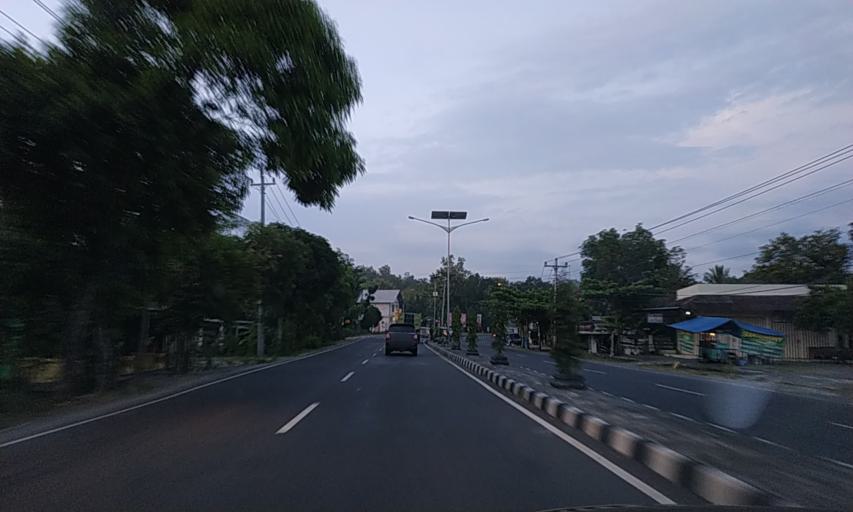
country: ID
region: Daerah Istimewa Yogyakarta
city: Srandakan
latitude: -7.8583
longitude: 110.2124
